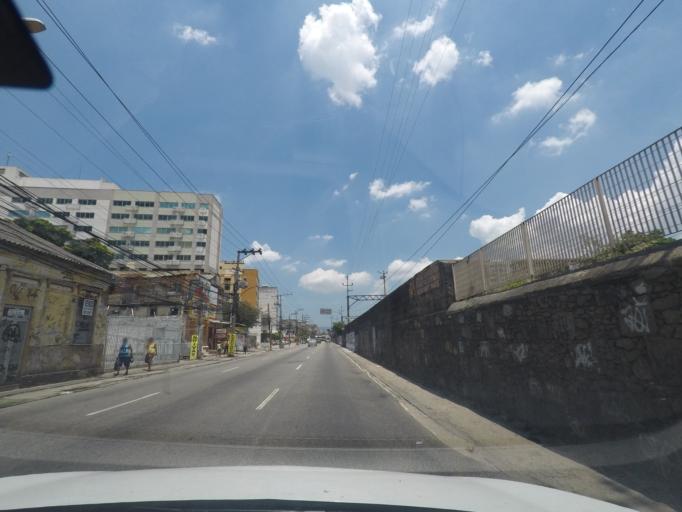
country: BR
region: Rio de Janeiro
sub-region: Sao Joao De Meriti
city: Sao Joao de Meriti
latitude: -22.8743
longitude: -43.3413
